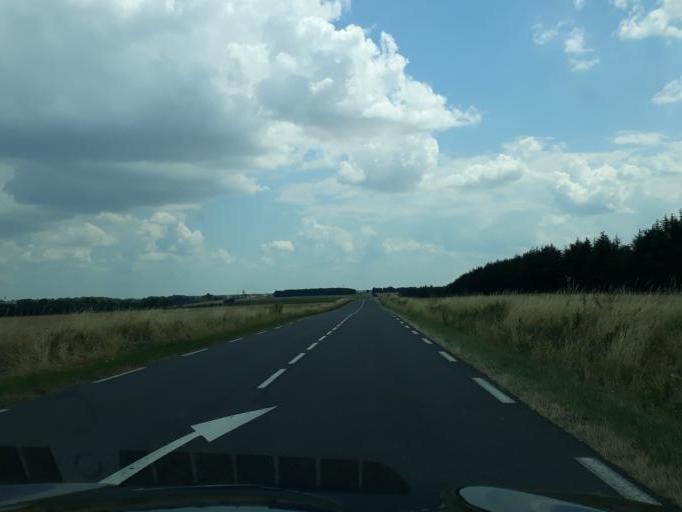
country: FR
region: Centre
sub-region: Departement du Cher
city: Avord
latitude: 47.0375
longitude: 2.6015
